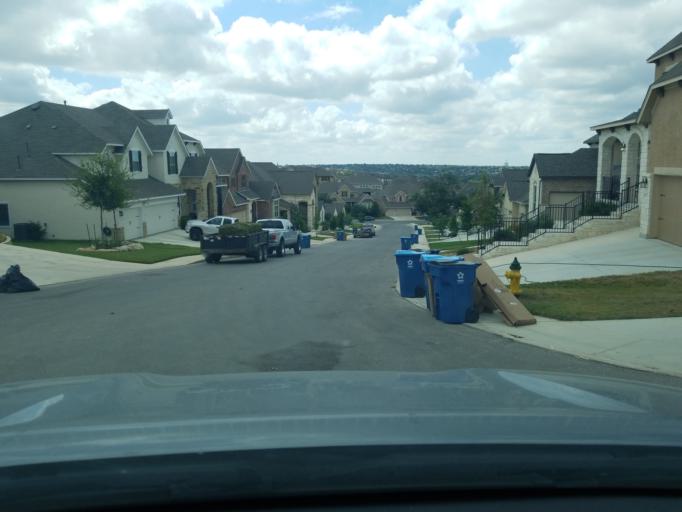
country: US
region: Texas
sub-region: Bexar County
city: Timberwood Park
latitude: 29.6667
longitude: -98.5122
